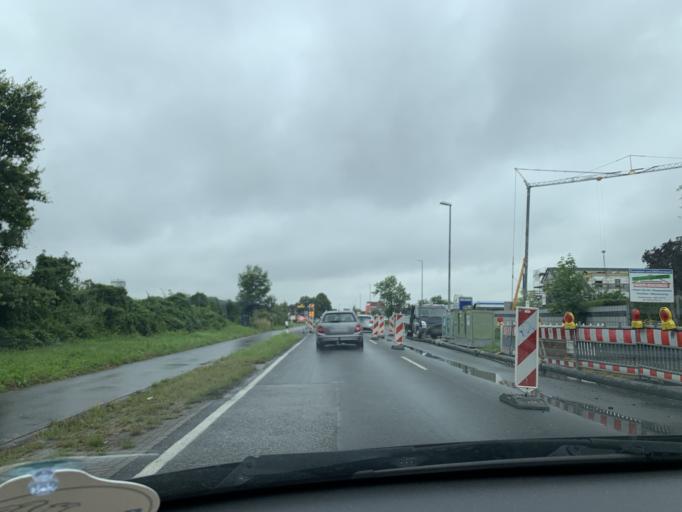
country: DE
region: North Rhine-Westphalia
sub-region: Regierungsbezirk Munster
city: Ochtrup
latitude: 52.2048
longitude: 7.2141
